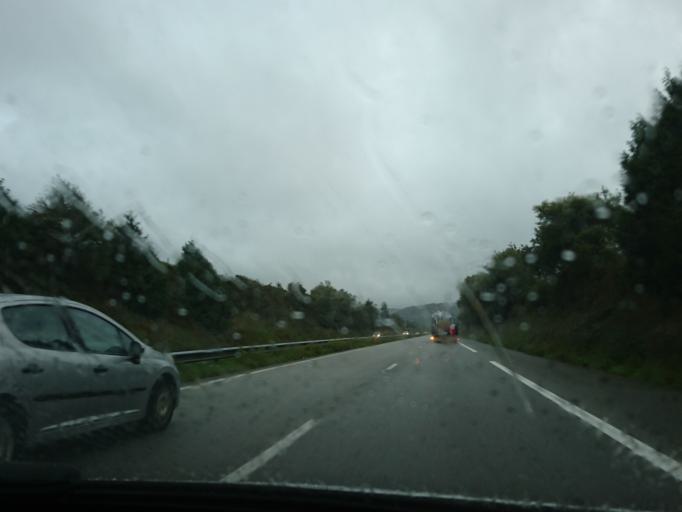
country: FR
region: Brittany
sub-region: Departement du Finistere
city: Chateaulin
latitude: 48.1972
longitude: -4.0445
